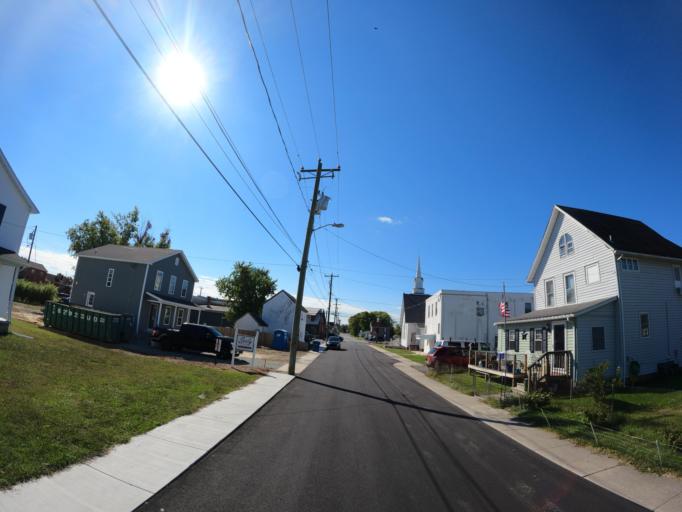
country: US
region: Delaware
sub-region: Sussex County
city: Bridgeville
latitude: 38.8083
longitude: -75.5936
